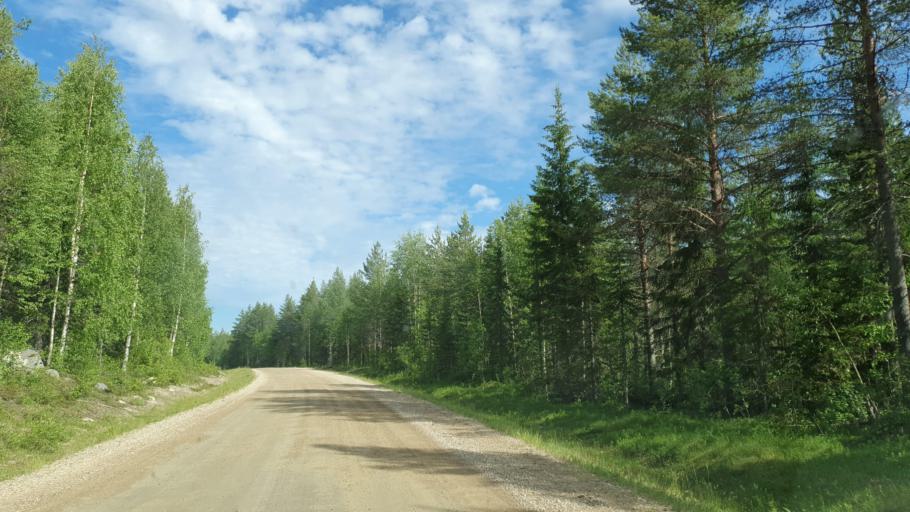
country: FI
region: Kainuu
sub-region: Kehys-Kainuu
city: Kuhmo
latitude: 64.5133
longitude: 29.4306
